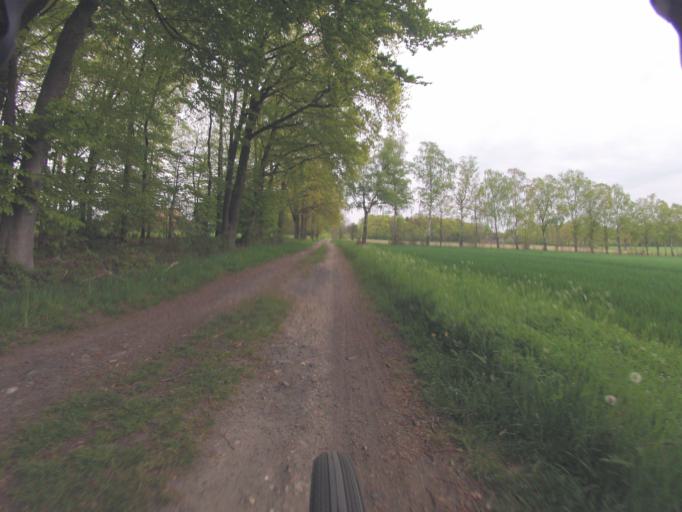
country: DE
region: North Rhine-Westphalia
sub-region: Regierungsbezirk Munster
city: Westerkappeln
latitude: 52.3017
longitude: 7.8455
